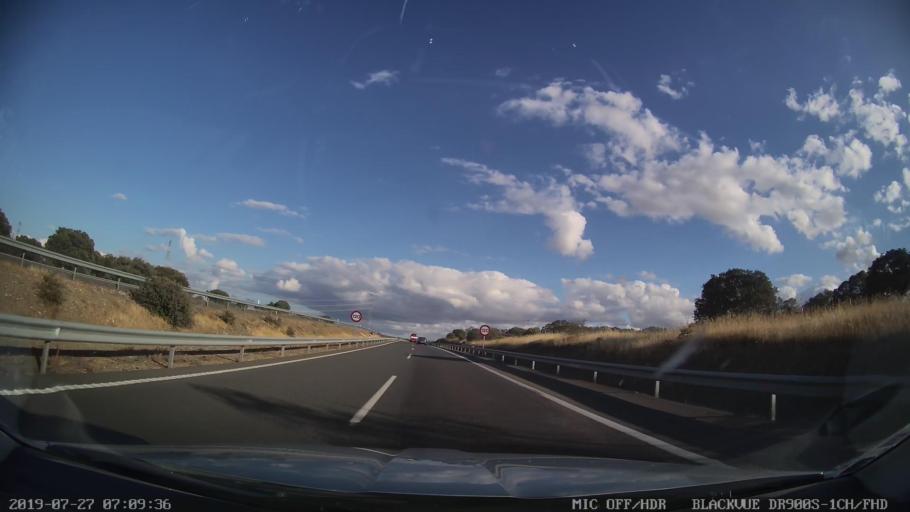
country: ES
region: Extremadura
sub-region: Provincia de Caceres
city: Jaraicejo
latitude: 39.5909
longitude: -5.8371
